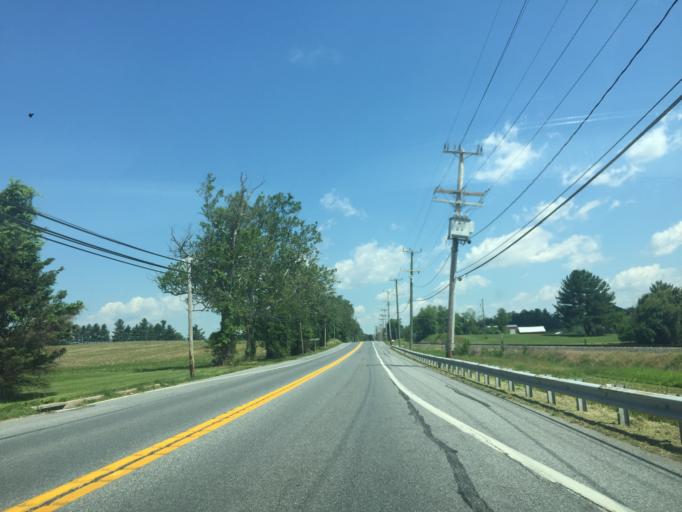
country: US
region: Maryland
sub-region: Baltimore County
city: Reisterstown
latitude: 39.4968
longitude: -76.8315
